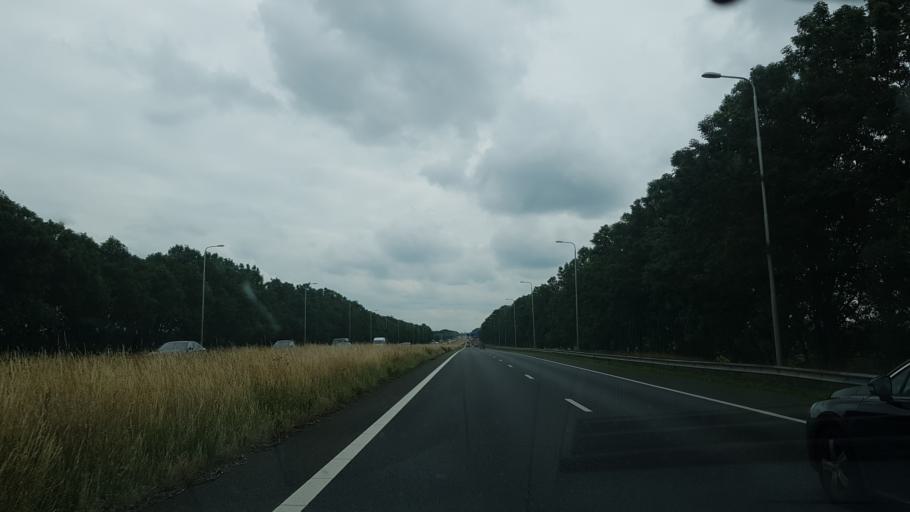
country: NL
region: North Holland
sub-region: Gemeente Beemster
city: Halfweg
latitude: 52.5545
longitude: 4.9615
